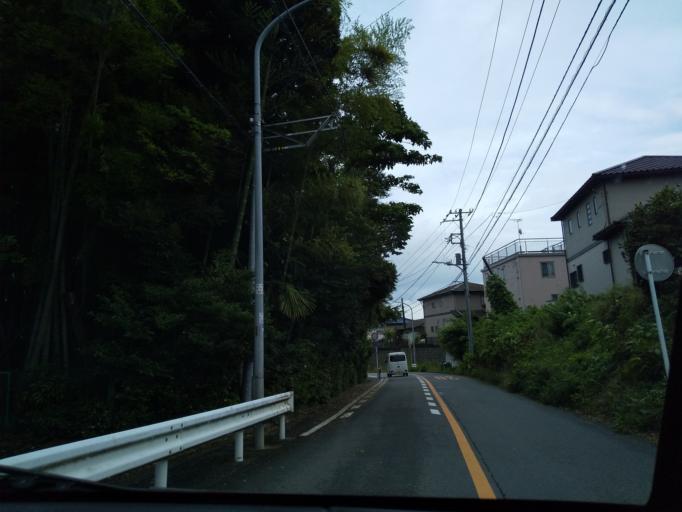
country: JP
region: Kanagawa
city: Fujisawa
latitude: 35.3730
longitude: 139.5167
